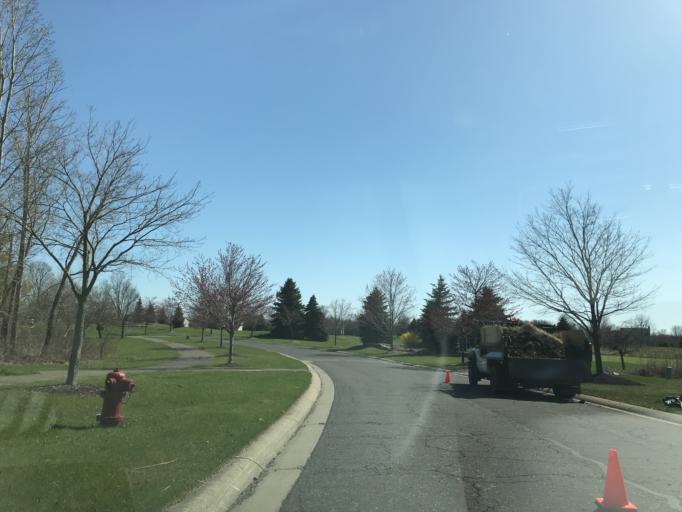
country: US
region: Michigan
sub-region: Oakland County
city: South Lyon
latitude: 42.4596
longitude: -83.5809
